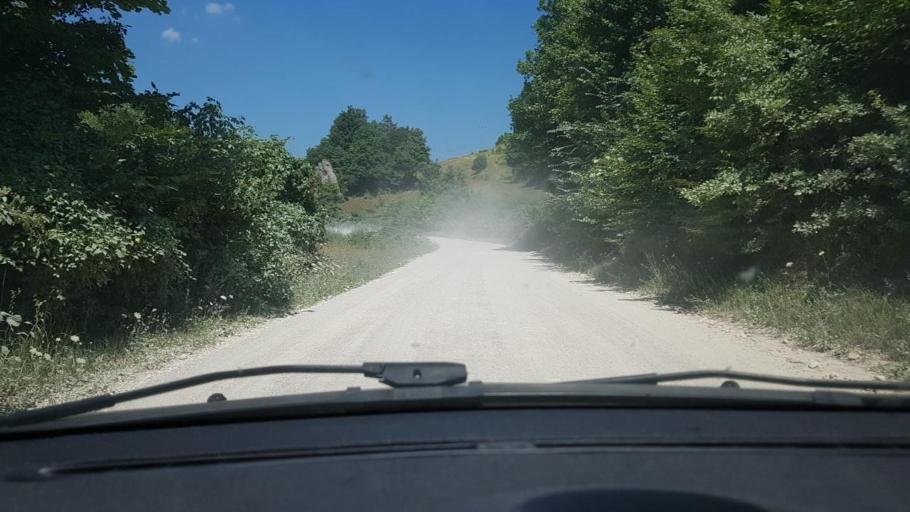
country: BA
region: Federation of Bosnia and Herzegovina
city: Orasac
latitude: 44.5063
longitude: 16.1289
